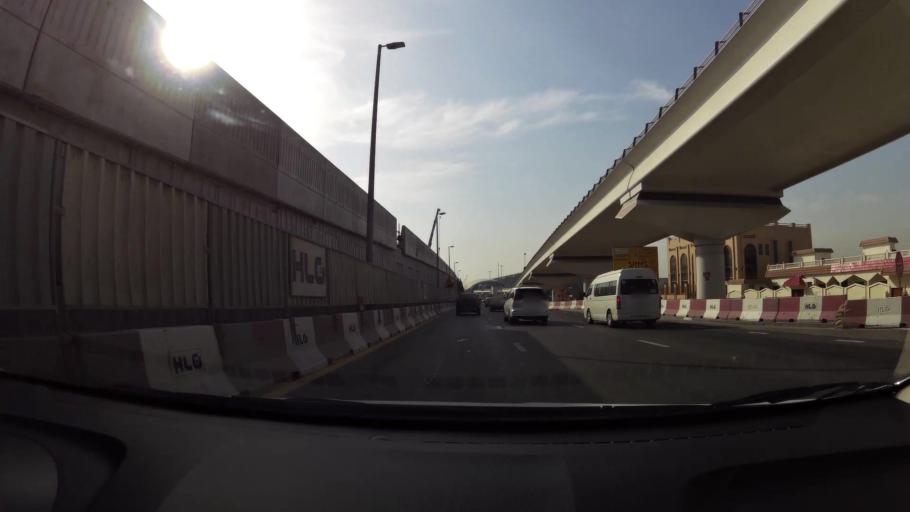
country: AE
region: Ash Shariqah
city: Sharjah
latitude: 25.2324
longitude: 55.3872
